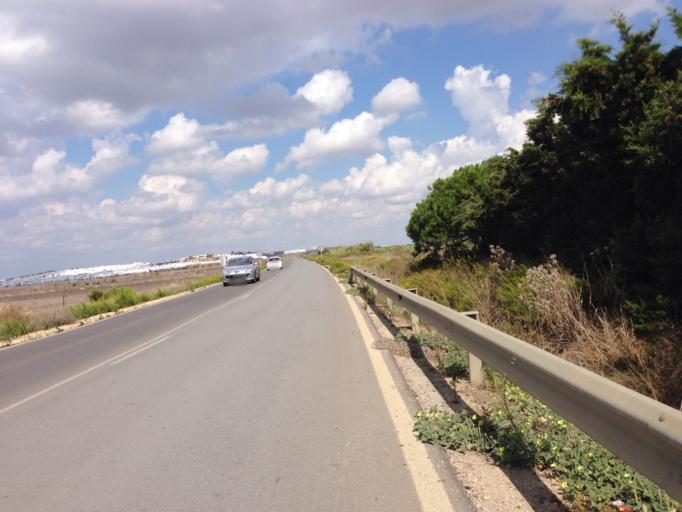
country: ES
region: Andalusia
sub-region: Provincia de Cadiz
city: Conil de la Frontera
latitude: 36.2533
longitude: -6.0693
